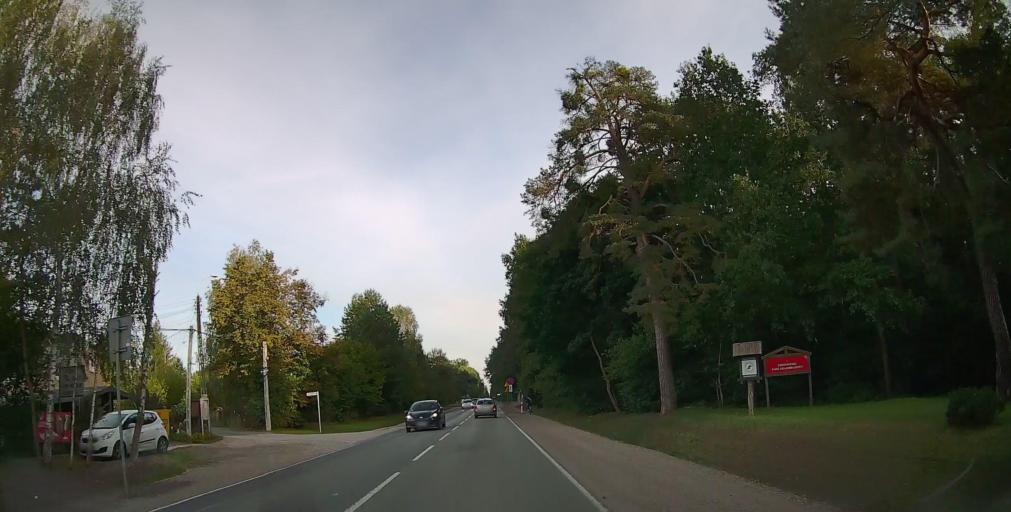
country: PL
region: Masovian Voivodeship
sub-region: Powiat piaseczynski
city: Zabieniec
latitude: 52.0529
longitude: 21.0602
